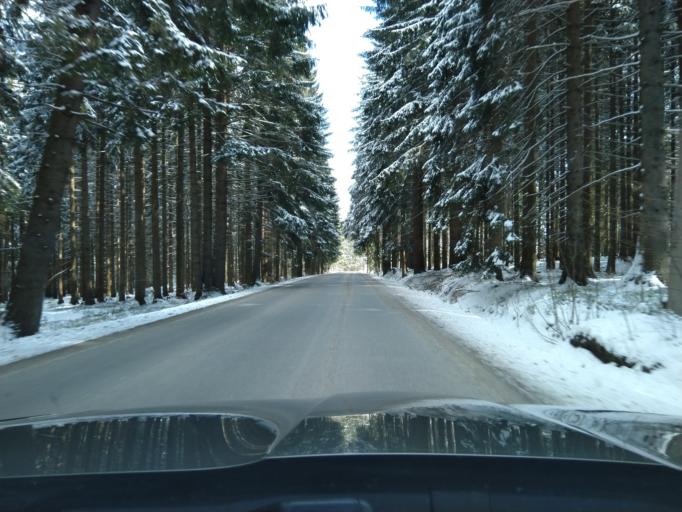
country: CZ
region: Jihocesky
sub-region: Okres Prachatice
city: Zdikov
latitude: 49.0602
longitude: 13.7212
